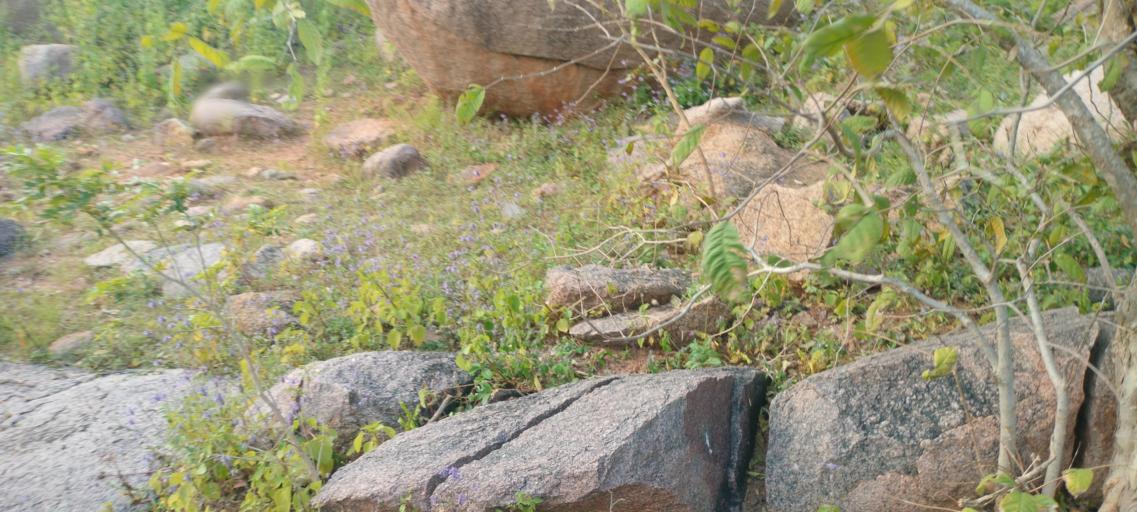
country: IN
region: Telangana
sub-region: Mahbubnagar
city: Farrukhnagar
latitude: 16.8964
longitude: 78.4908
